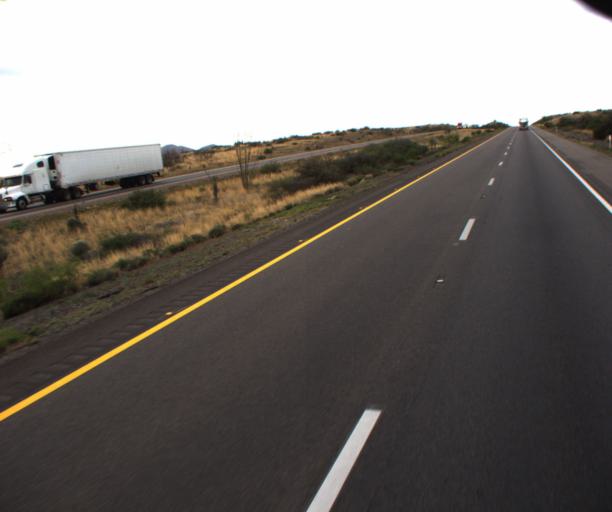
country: US
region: Arizona
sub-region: Cochise County
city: Willcox
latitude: 32.1386
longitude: -110.0030
